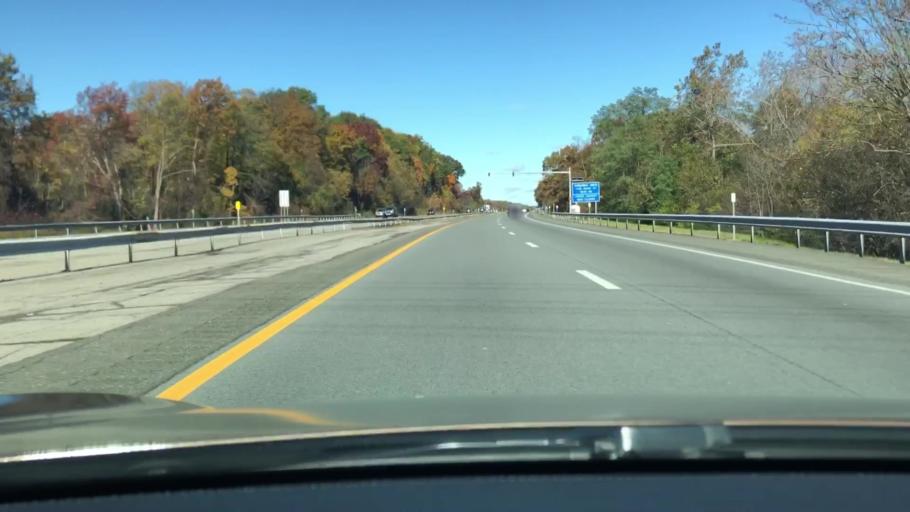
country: US
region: New York
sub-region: Orange County
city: Vails Gate
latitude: 41.4864
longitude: -74.0794
